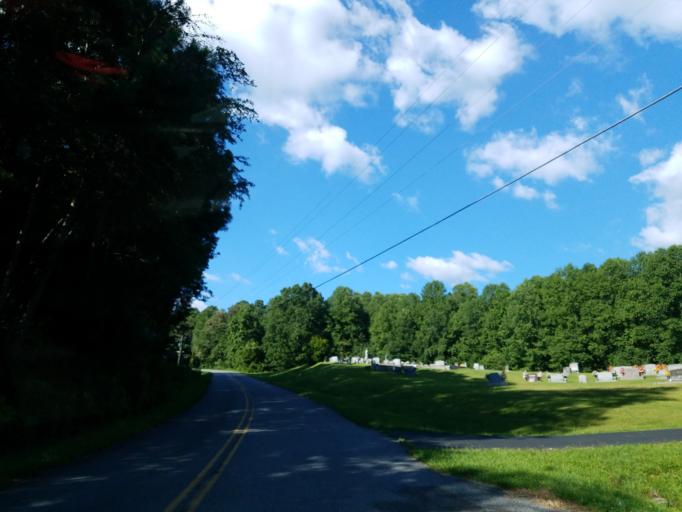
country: US
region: Georgia
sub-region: Gilmer County
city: Ellijay
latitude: 34.6762
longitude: -84.3281
